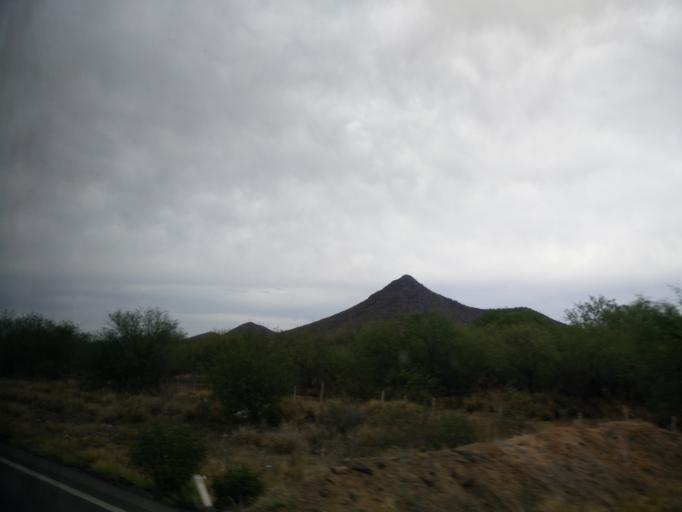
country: MX
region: Sonora
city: Hermosillo
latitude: 28.8100
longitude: -110.9579
